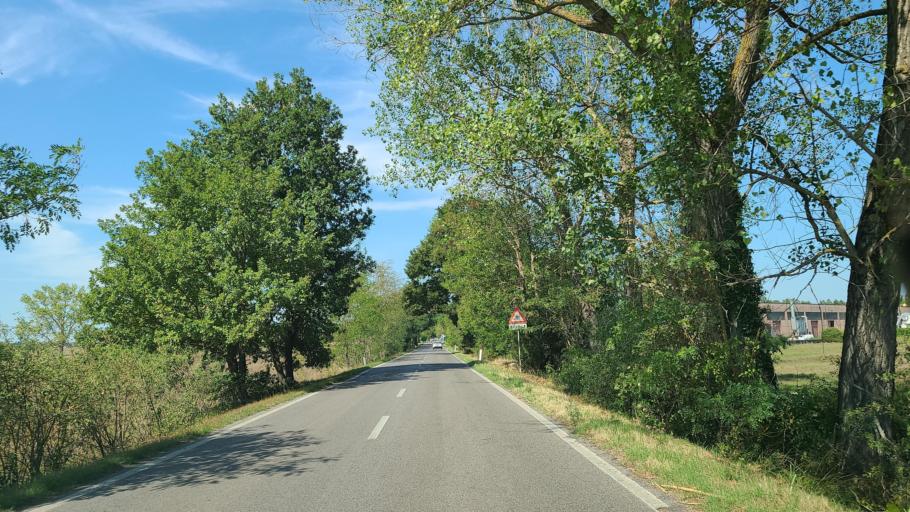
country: IT
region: Tuscany
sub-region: Provincia di Siena
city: Castellina Scalo
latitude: 43.3931
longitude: 11.1980
